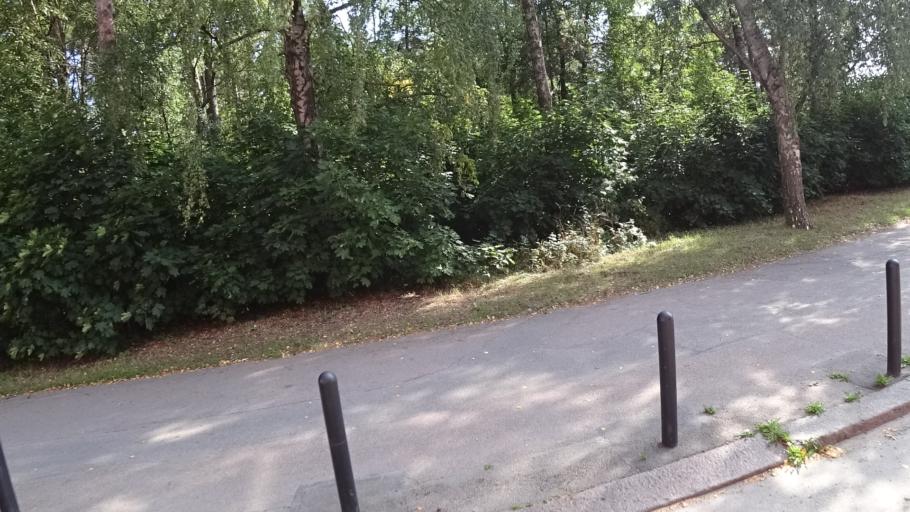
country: FI
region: Kymenlaakso
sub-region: Kotka-Hamina
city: Kotka
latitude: 60.4613
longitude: 26.9272
